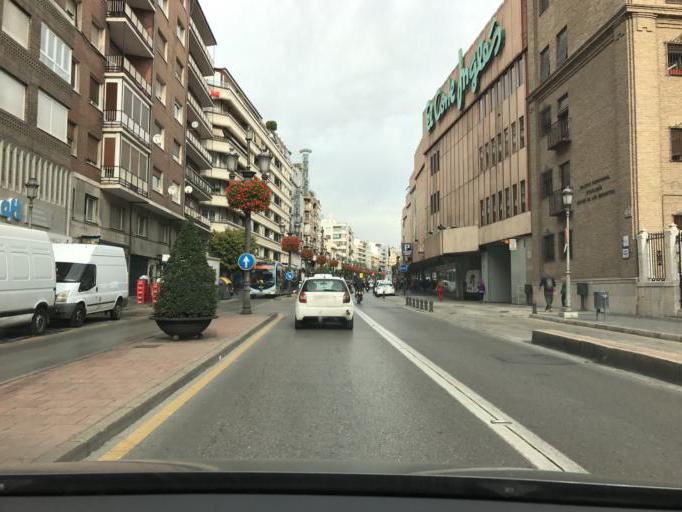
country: ES
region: Andalusia
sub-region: Provincia de Granada
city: Granada
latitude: 37.1697
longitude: -3.5975
